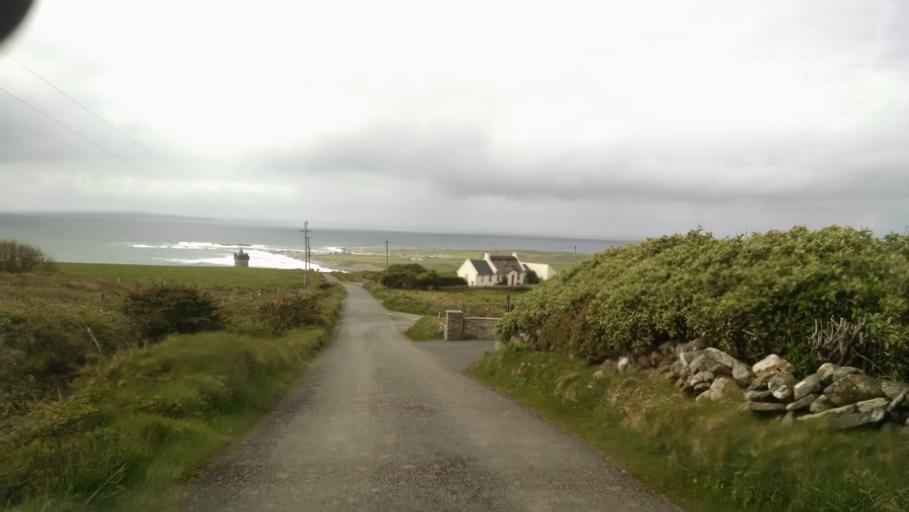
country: IE
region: Connaught
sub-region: County Galway
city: Bearna
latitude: 53.0015
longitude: -9.3827
